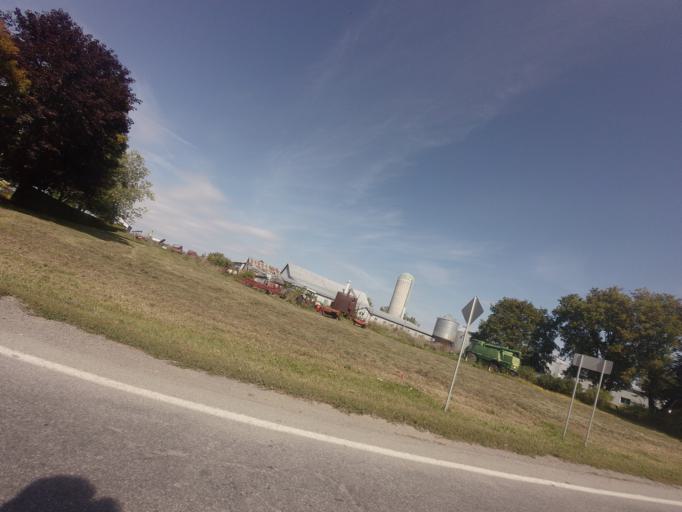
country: CA
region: Quebec
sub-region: Laurentides
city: Saint-Eustache
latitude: 45.5931
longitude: -73.9070
